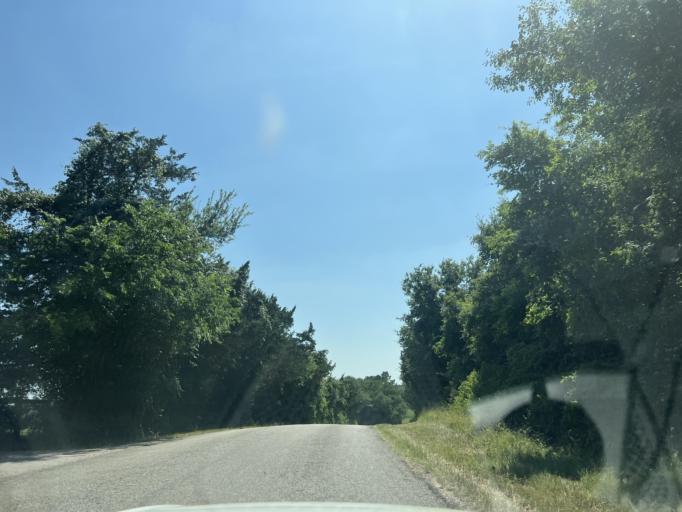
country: US
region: Texas
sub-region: Washington County
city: Brenham
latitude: 30.1546
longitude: -96.4713
